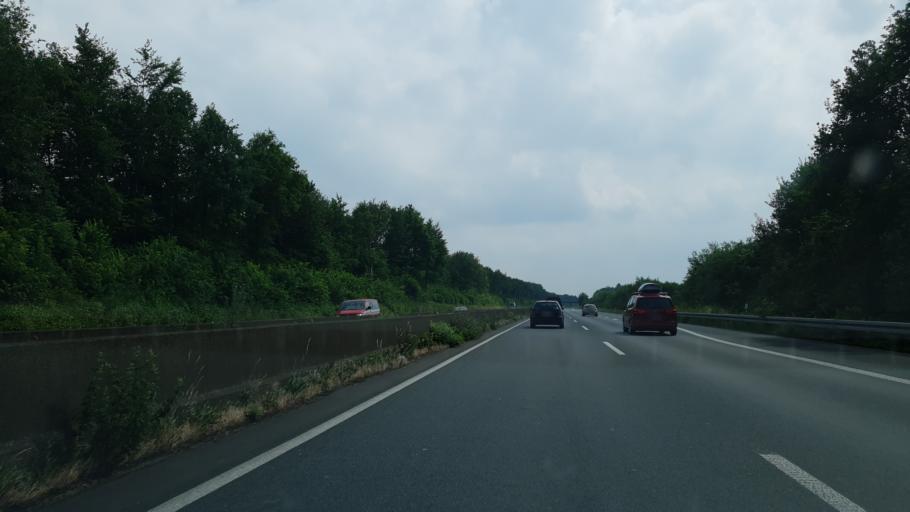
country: DE
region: North Rhine-Westphalia
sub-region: Regierungsbezirk Munster
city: Velen
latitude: 51.9036
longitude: 7.0256
